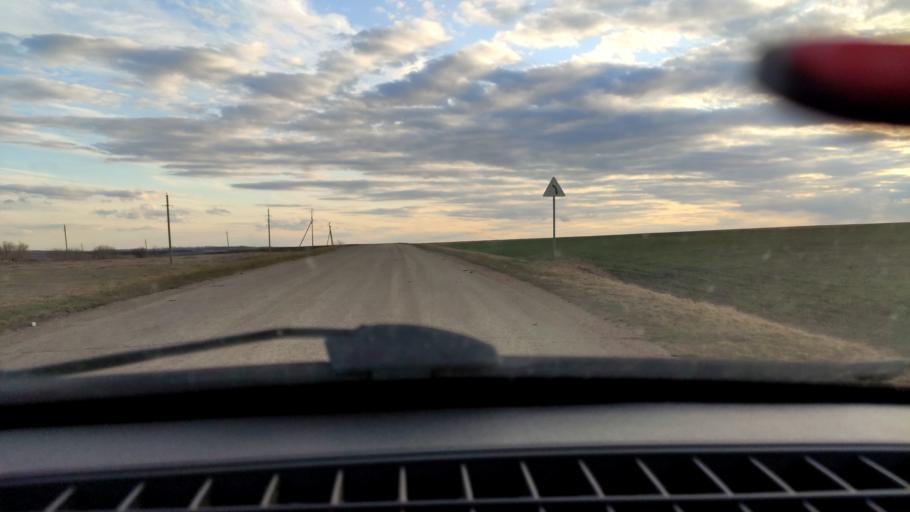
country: RU
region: Bashkortostan
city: Tolbazy
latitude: 54.0026
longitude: 55.6806
